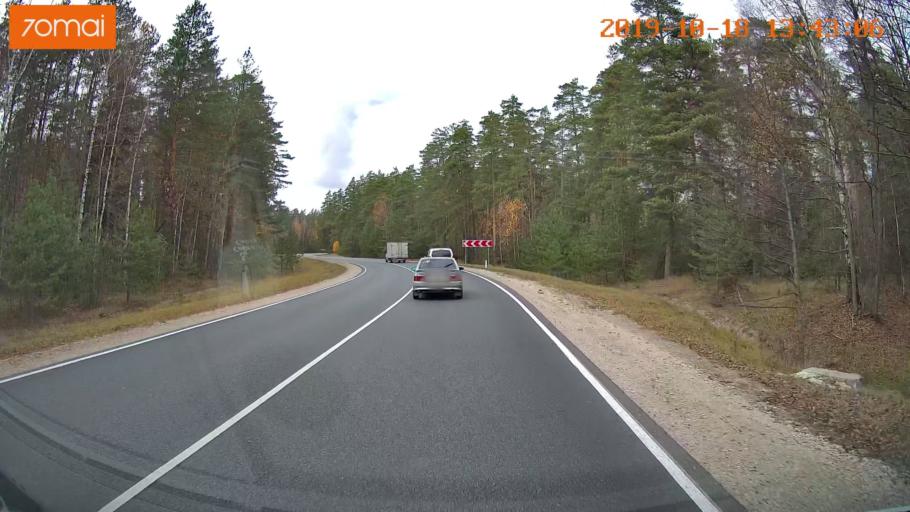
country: RU
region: Rjazan
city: Solotcha
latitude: 54.9281
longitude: 39.9786
